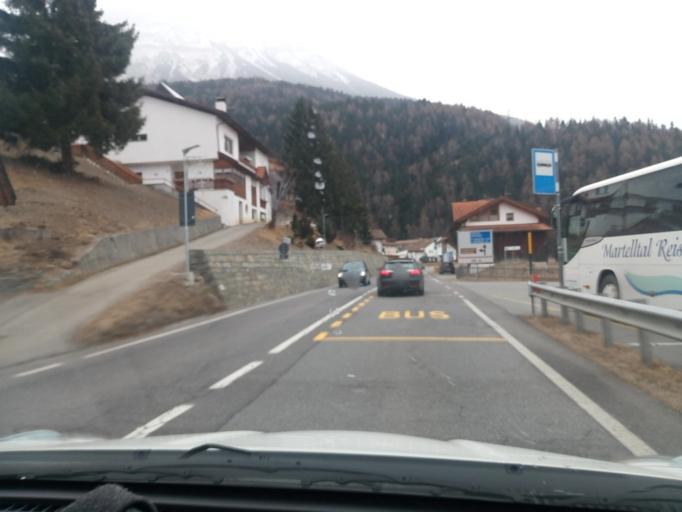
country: IT
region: Trentino-Alto Adige
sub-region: Bolzano
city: Curon Venosta
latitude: 46.8083
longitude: 10.5405
